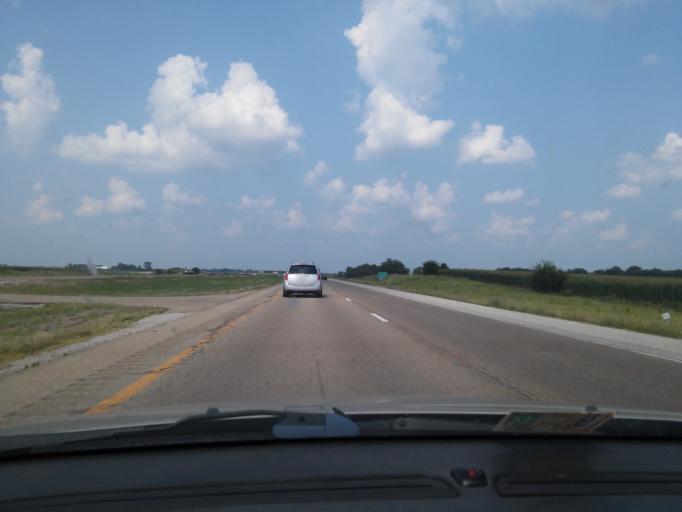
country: US
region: Illinois
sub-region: McLean County
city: Chenoa
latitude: 40.7550
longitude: -88.7297
